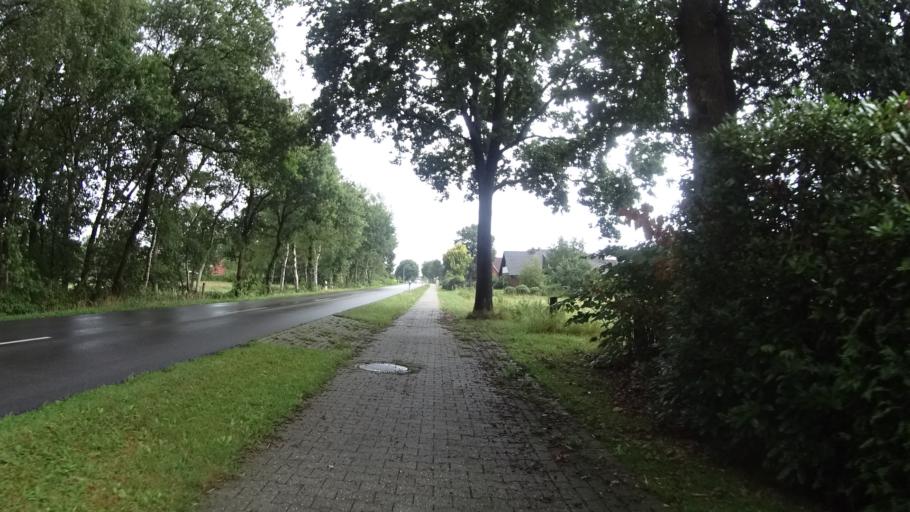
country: DE
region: Lower Saxony
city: Schwerinsdorf
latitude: 53.3457
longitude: 7.7360
